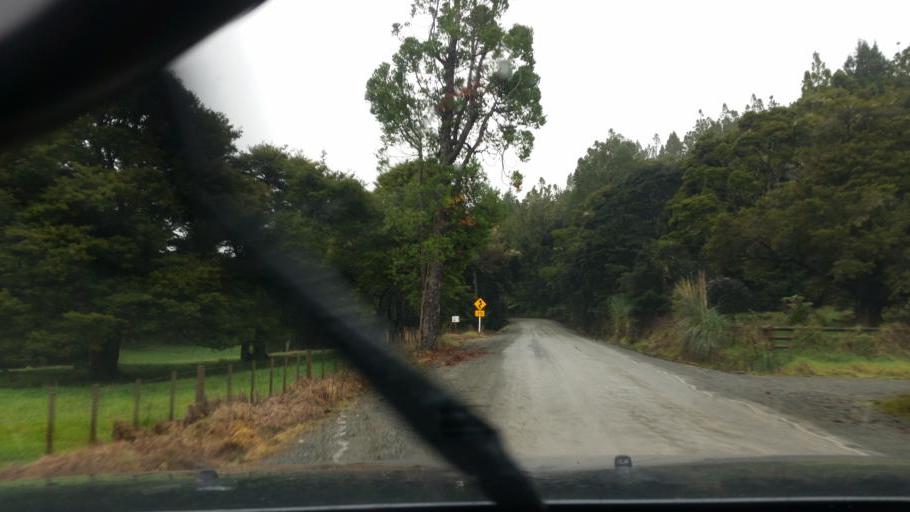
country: NZ
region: Auckland
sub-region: Auckland
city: Wellsford
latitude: -36.1012
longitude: 174.5059
